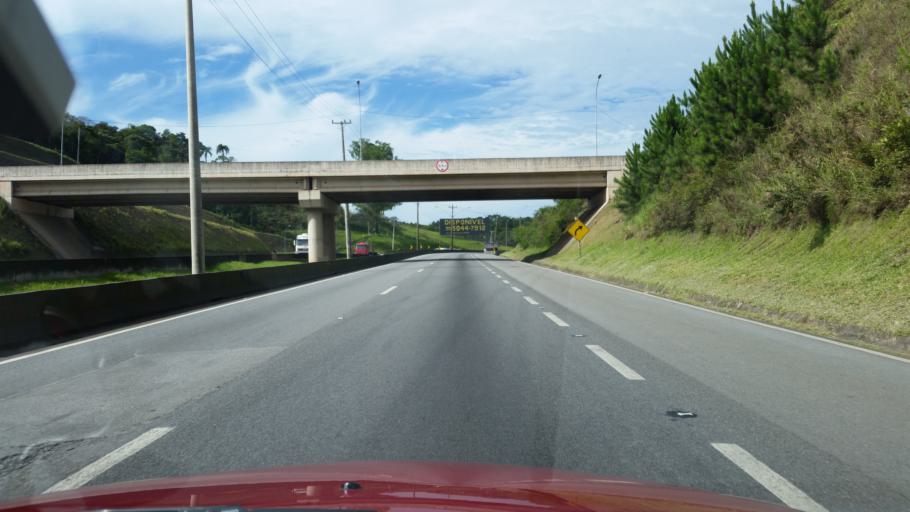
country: BR
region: Sao Paulo
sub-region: Sao Lourenco Da Serra
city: Sao Lourenco da Serra
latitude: -23.8011
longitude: -46.9170
